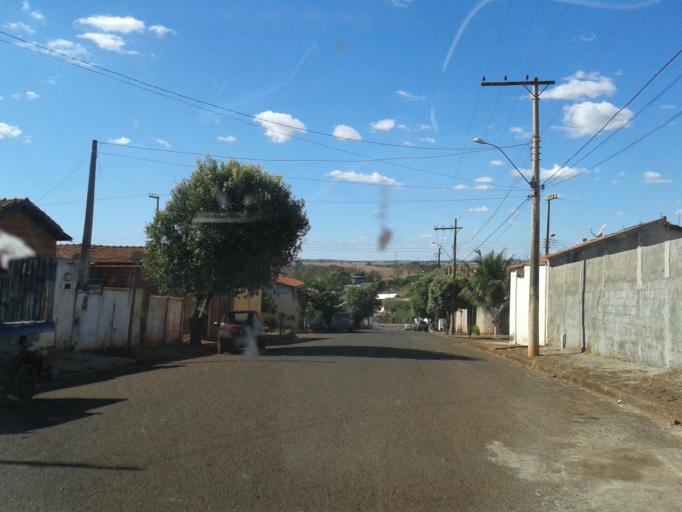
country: BR
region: Minas Gerais
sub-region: Ituiutaba
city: Ituiutaba
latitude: -18.9549
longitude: -49.4583
